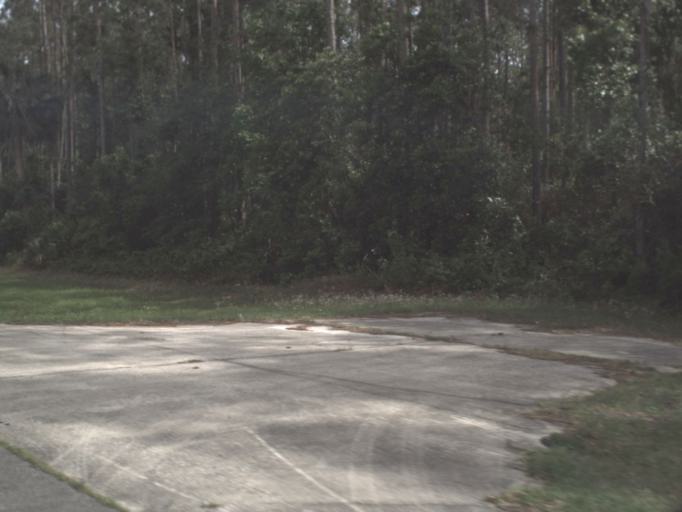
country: US
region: Florida
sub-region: Flagler County
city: Bunnell
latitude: 29.4772
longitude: -81.3354
